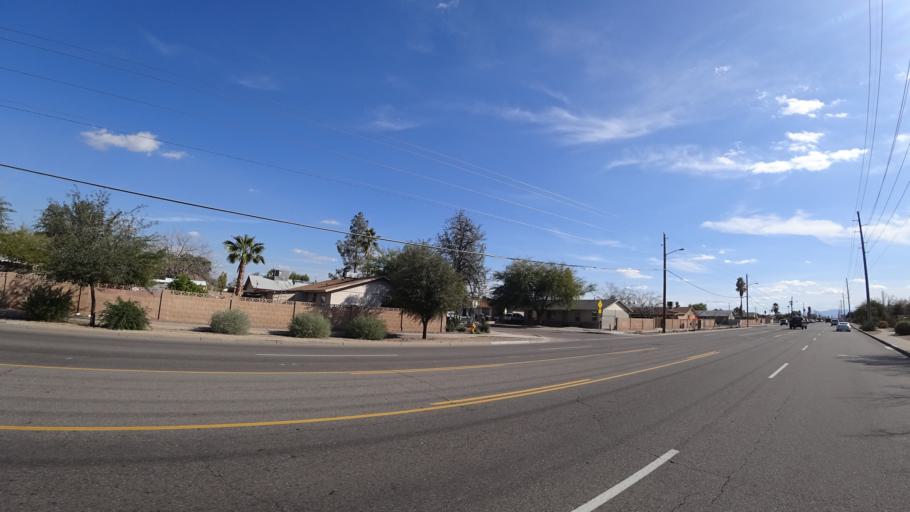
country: US
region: Arizona
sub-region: Maricopa County
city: Peoria
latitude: 33.5867
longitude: -112.2203
